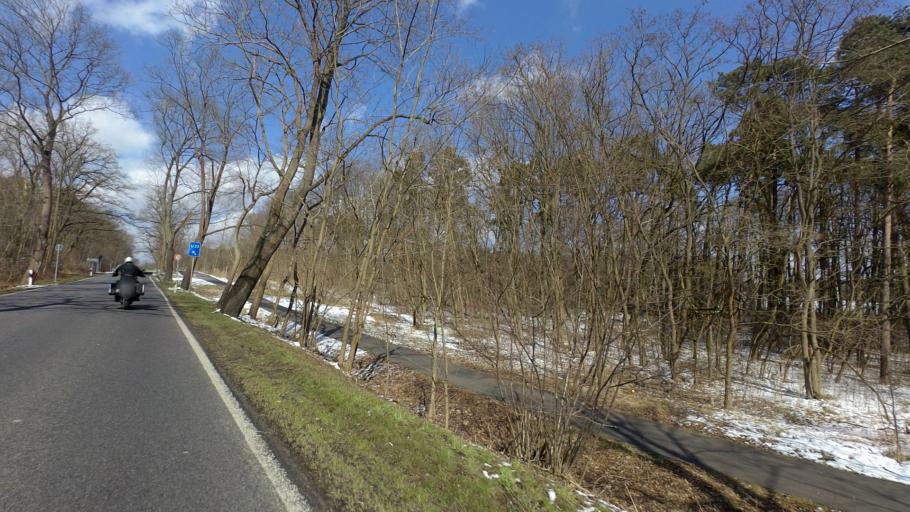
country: DE
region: Brandenburg
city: Britz
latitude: 52.8899
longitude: 13.7209
